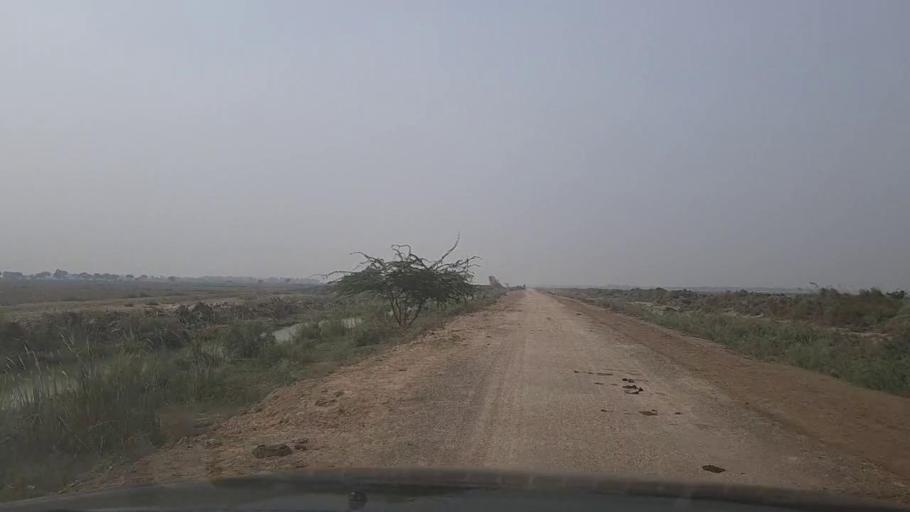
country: PK
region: Sindh
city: Mirpur Sakro
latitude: 24.5319
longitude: 67.7867
